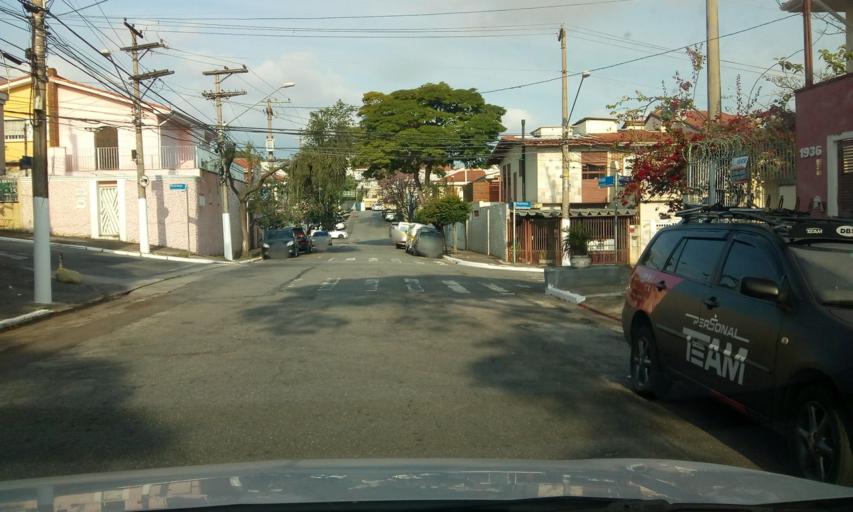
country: BR
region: Sao Paulo
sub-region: Diadema
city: Diadema
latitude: -23.6202
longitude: -46.6529
